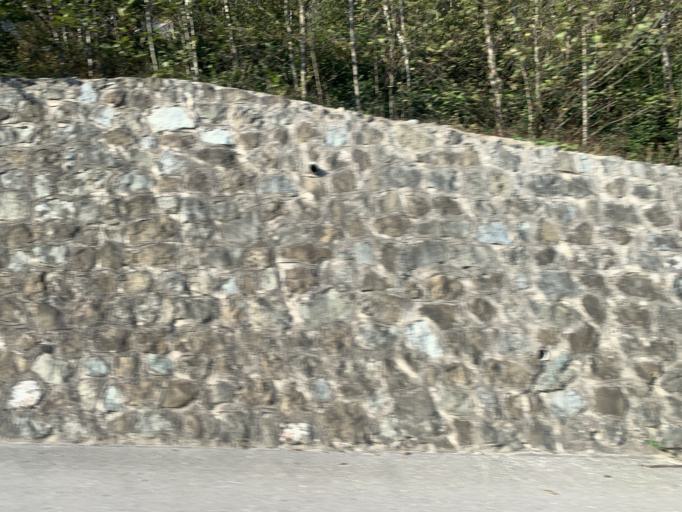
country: TR
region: Trabzon
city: Dernekpazari
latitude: 40.8366
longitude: 40.2734
